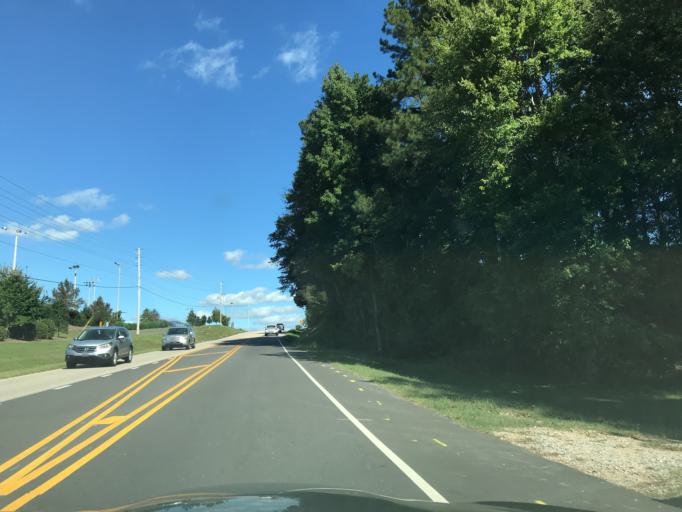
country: US
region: North Carolina
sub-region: Wake County
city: Wake Forest
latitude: 35.9396
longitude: -78.5075
